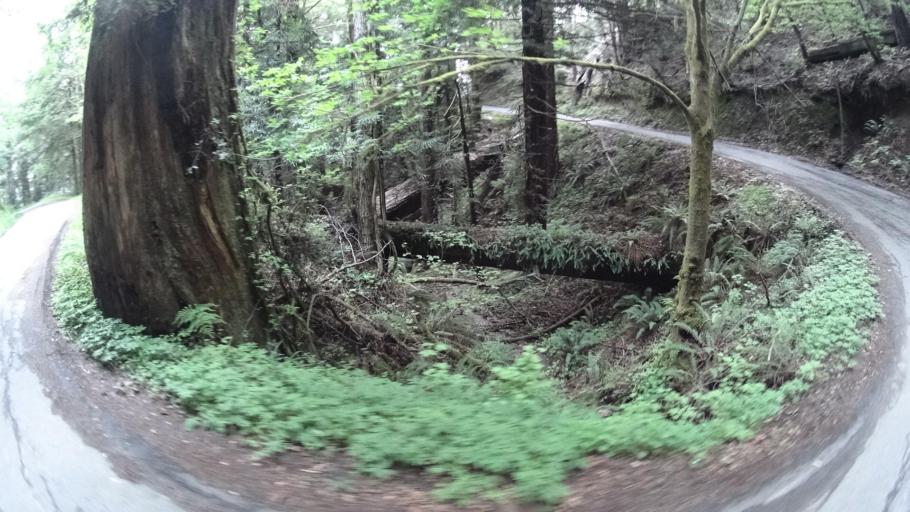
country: US
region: California
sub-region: Humboldt County
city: Redway
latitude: 40.3370
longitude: -123.9114
